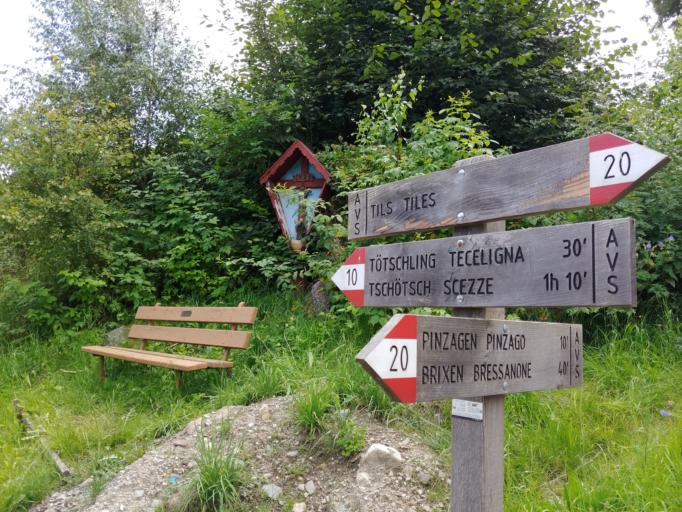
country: IT
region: Trentino-Alto Adige
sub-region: Bolzano
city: Bressanone
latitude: 46.7097
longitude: 11.6312
